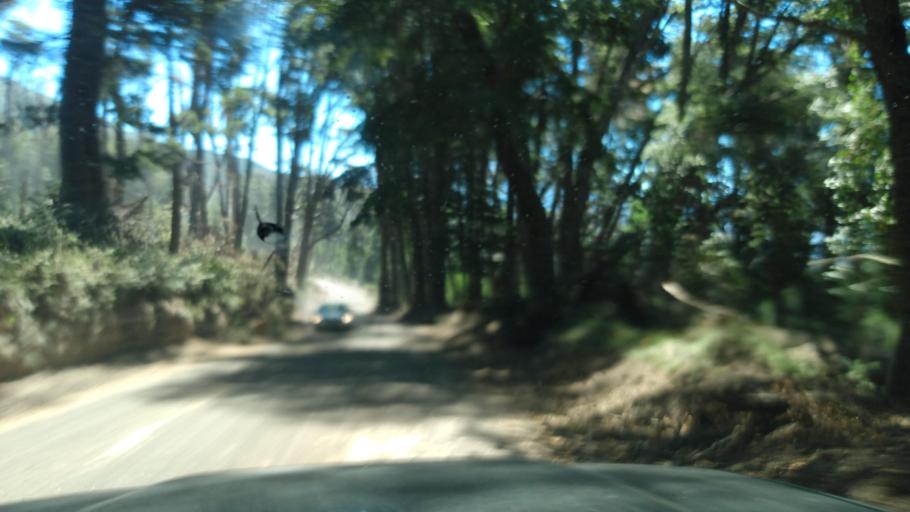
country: AR
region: Neuquen
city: Villa La Angostura
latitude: -40.6501
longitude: -71.4287
